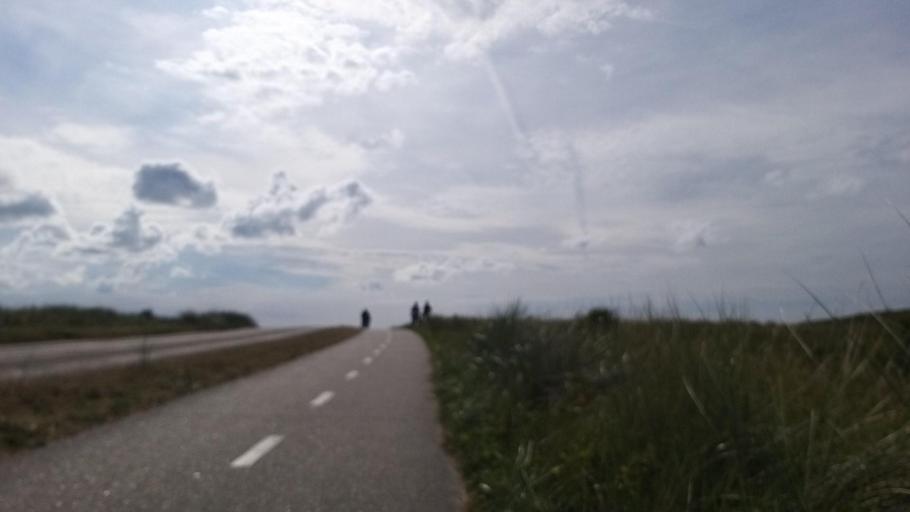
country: NL
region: North Holland
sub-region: Gemeente Texel
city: Den Burg
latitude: 53.1586
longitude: 4.8374
